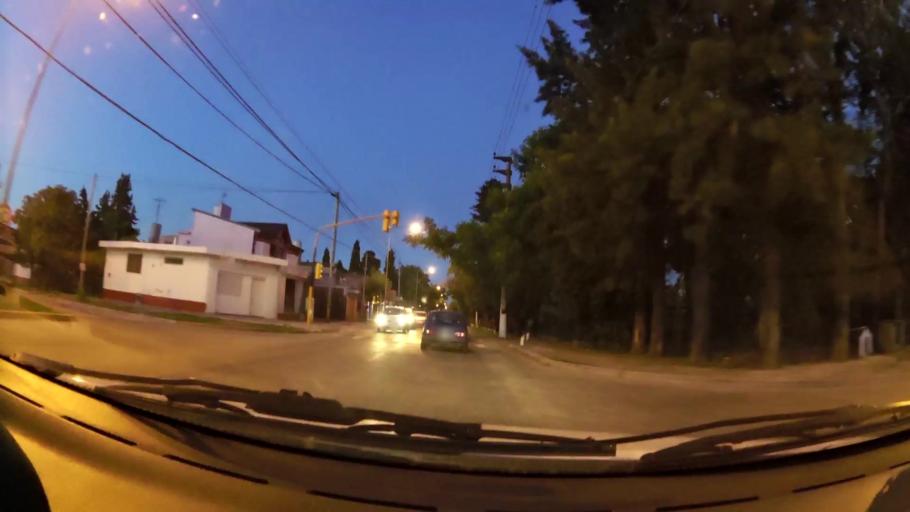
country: AR
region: Buenos Aires
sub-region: Partido de Quilmes
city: Quilmes
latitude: -34.7839
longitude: -58.1843
